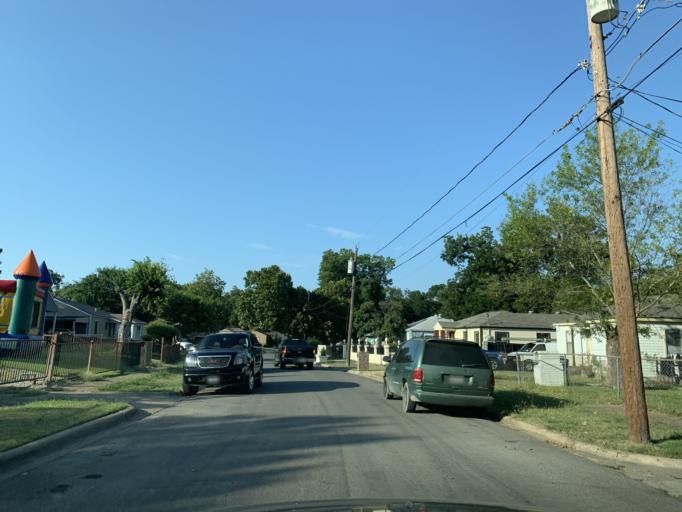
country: US
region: Texas
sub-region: Dallas County
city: Dallas
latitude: 32.7114
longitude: -96.7893
